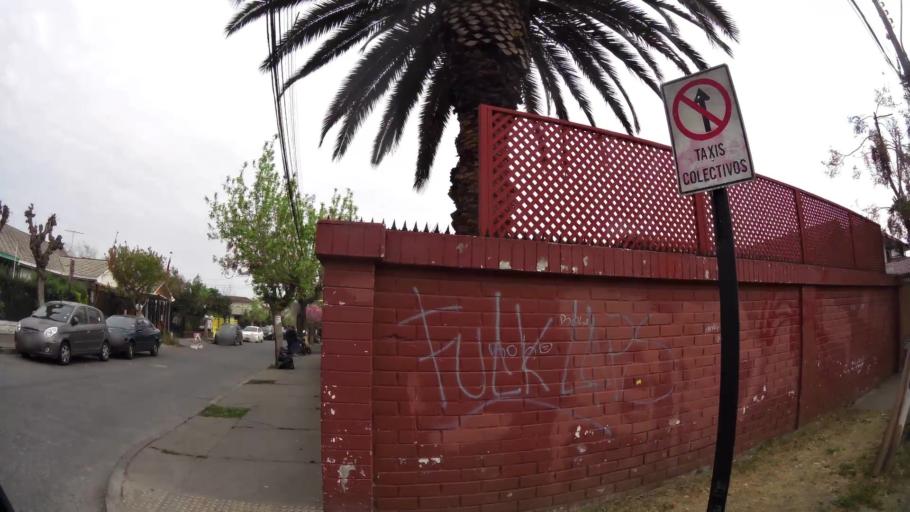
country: CL
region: Santiago Metropolitan
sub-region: Provincia de Santiago
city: Lo Prado
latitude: -33.5113
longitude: -70.7547
